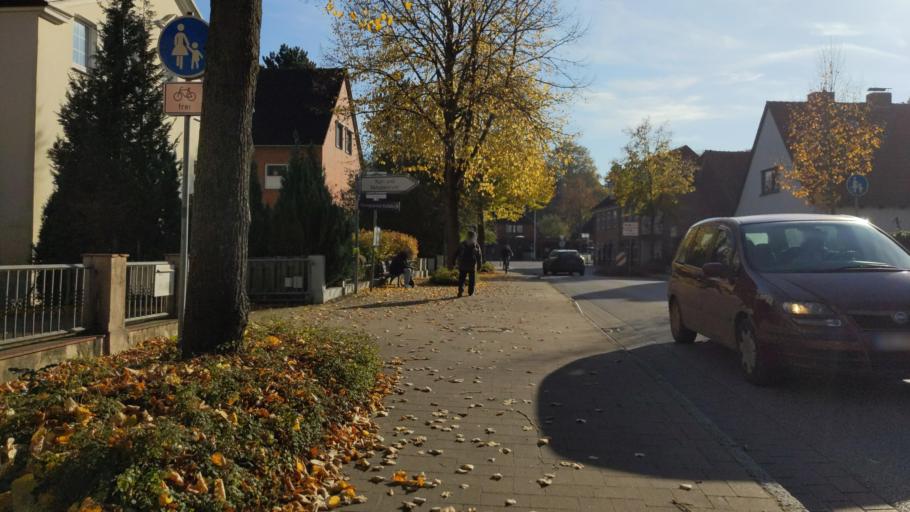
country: DE
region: Schleswig-Holstein
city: Eutin
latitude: 54.1428
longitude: 10.6124
